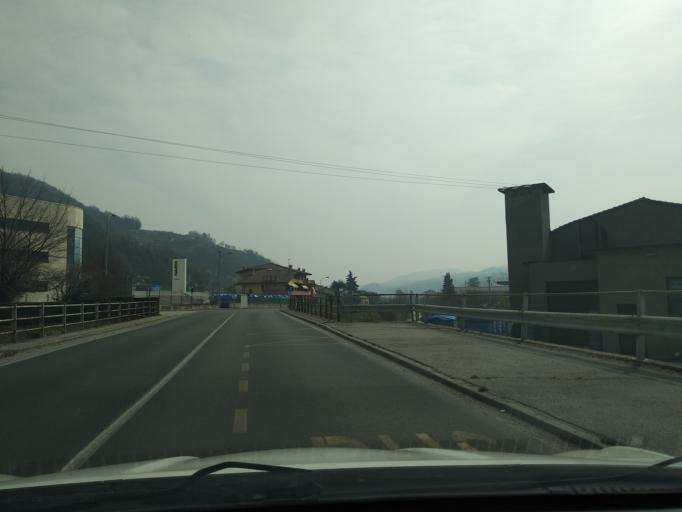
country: IT
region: Veneto
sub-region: Provincia di Vicenza
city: Chiampo
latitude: 45.5554
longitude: 11.2717
